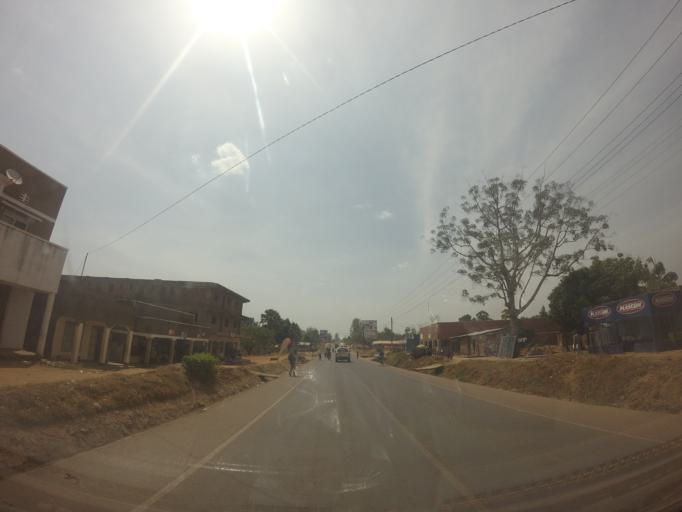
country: UG
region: Northern Region
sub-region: Arua District
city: Arua
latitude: 3.0049
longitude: 30.9115
